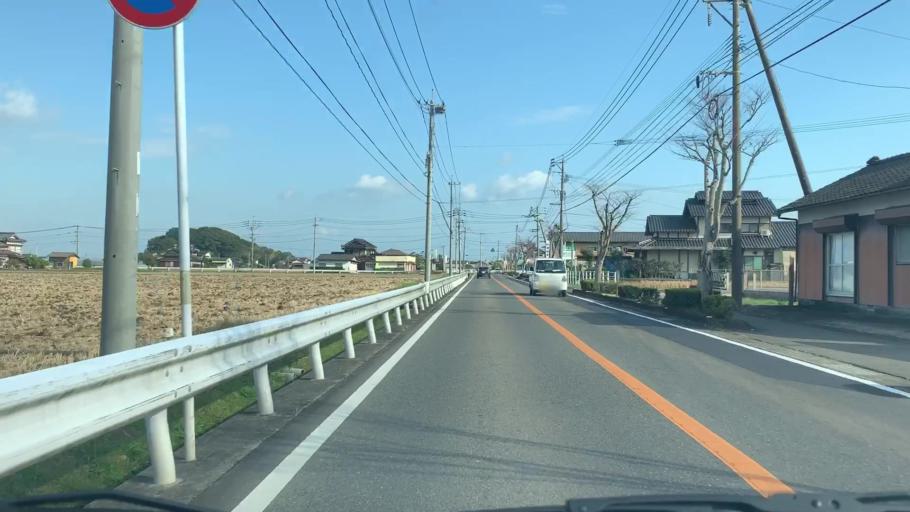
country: JP
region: Saga Prefecture
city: Kashima
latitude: 33.1239
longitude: 130.0772
